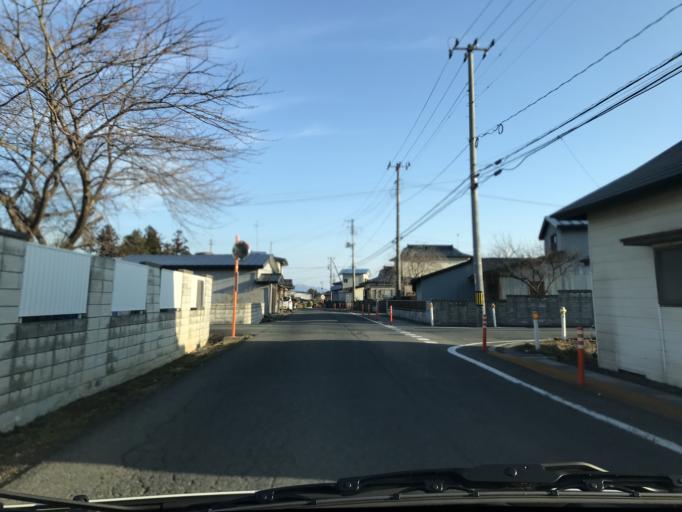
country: JP
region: Iwate
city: Kitakami
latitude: 39.2122
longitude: 141.1143
